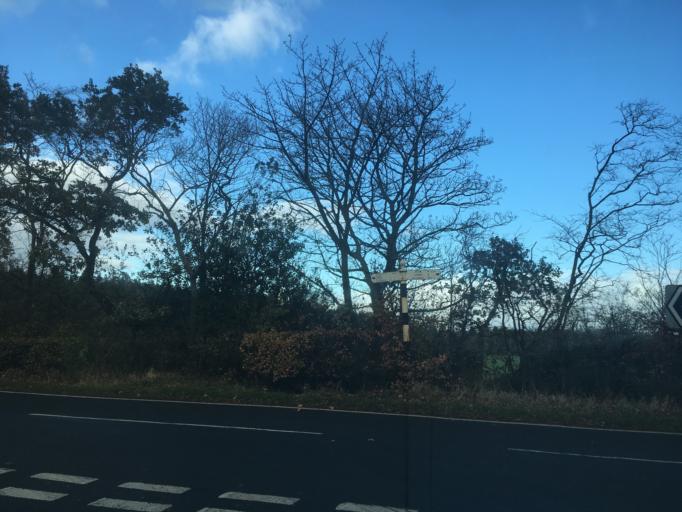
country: GB
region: Scotland
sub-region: East Lothian
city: Pencaitland
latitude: 55.8448
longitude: -2.8716
